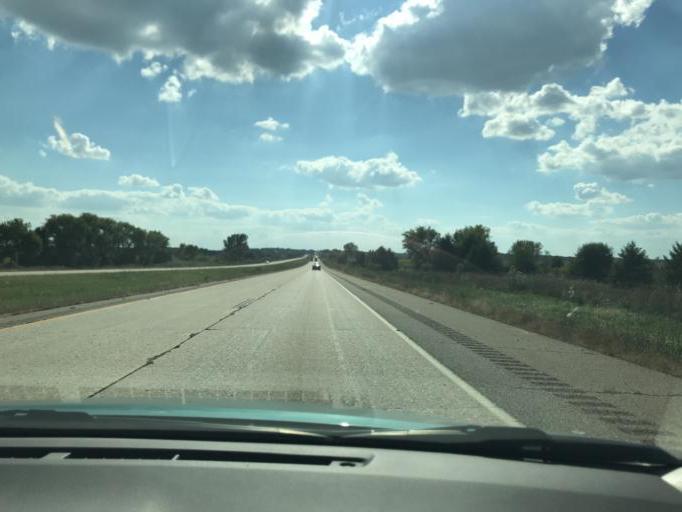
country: US
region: Wisconsin
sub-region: Walworth County
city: Darien
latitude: 42.6003
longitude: -88.7378
